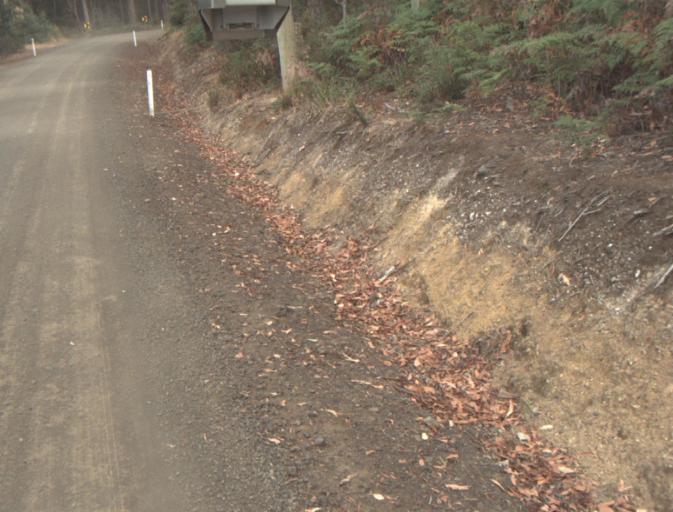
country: AU
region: Tasmania
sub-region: Launceston
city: Mayfield
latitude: -41.2166
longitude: 147.1699
